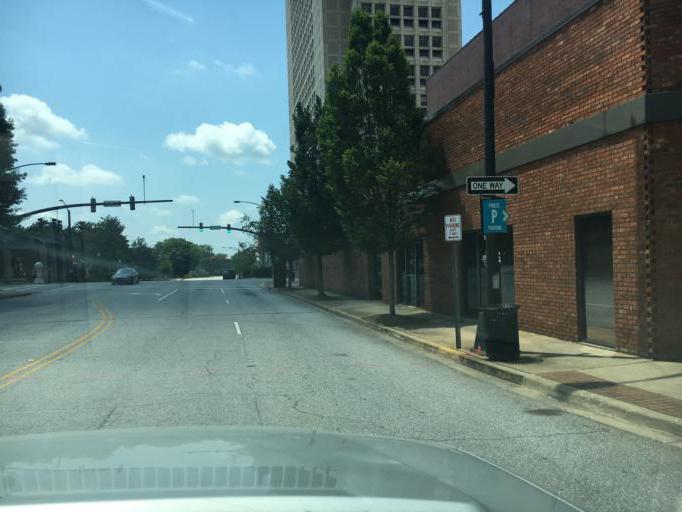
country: US
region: South Carolina
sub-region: Spartanburg County
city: Spartanburg
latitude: 34.9510
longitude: -81.9282
